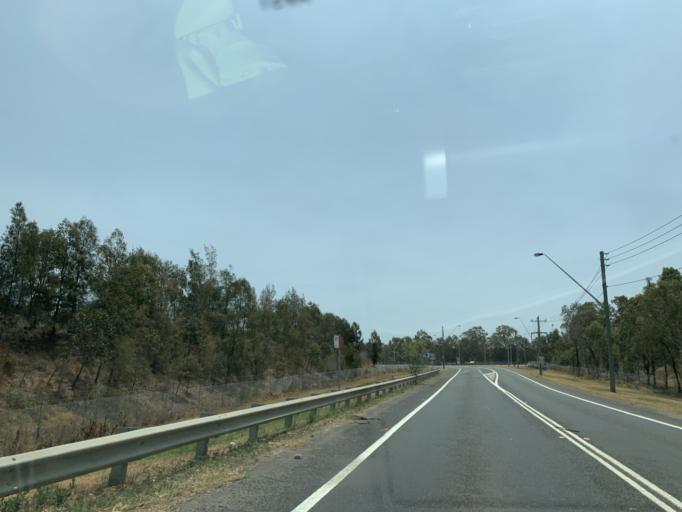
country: AU
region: New South Wales
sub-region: Fairfield
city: Horsley Park
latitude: -33.8189
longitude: 150.8673
